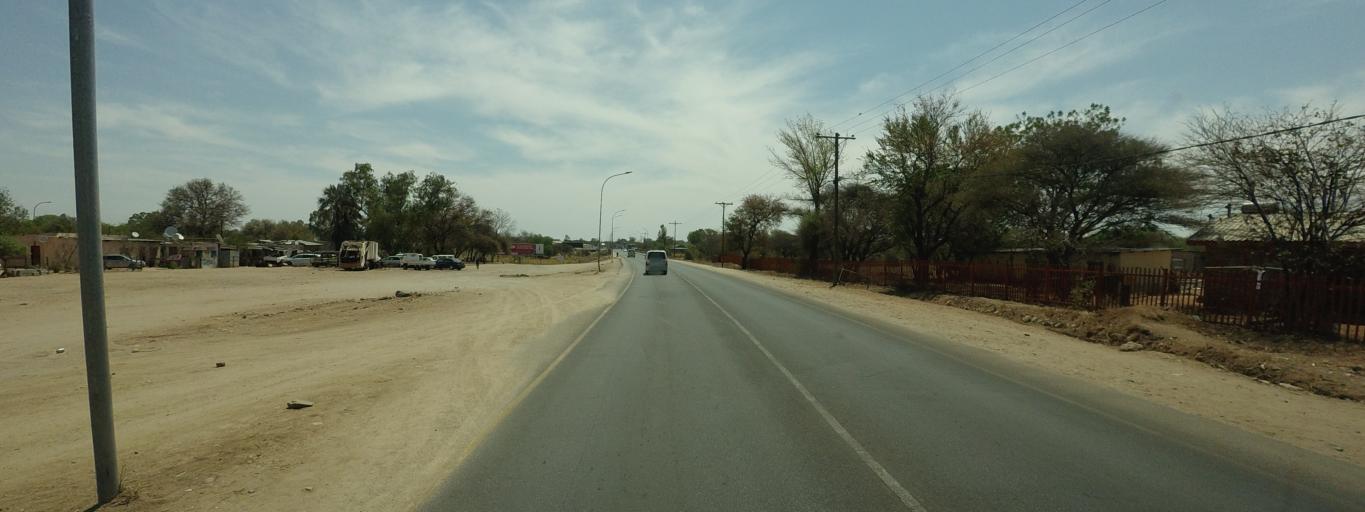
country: BW
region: North East
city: Francistown
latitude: -21.1713
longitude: 27.5020
